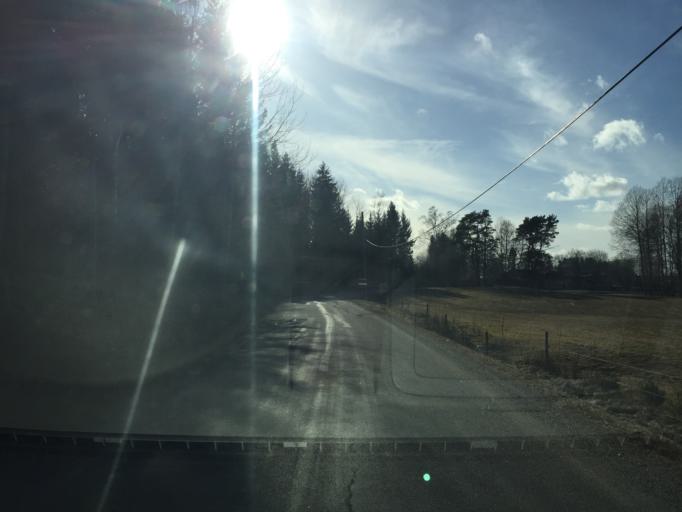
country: SE
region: Stockholm
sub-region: Nynashamns Kommun
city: Osmo
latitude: 59.0454
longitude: 17.8302
